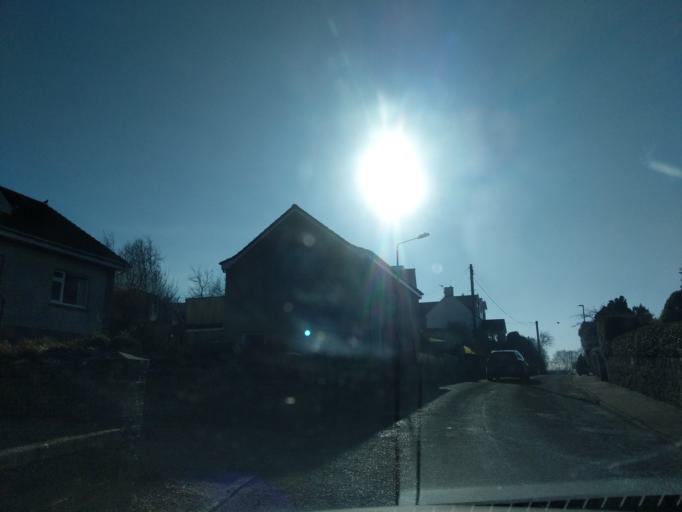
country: GB
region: Scotland
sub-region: South Lanarkshire
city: Lanark
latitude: 55.6678
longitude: -3.7752
